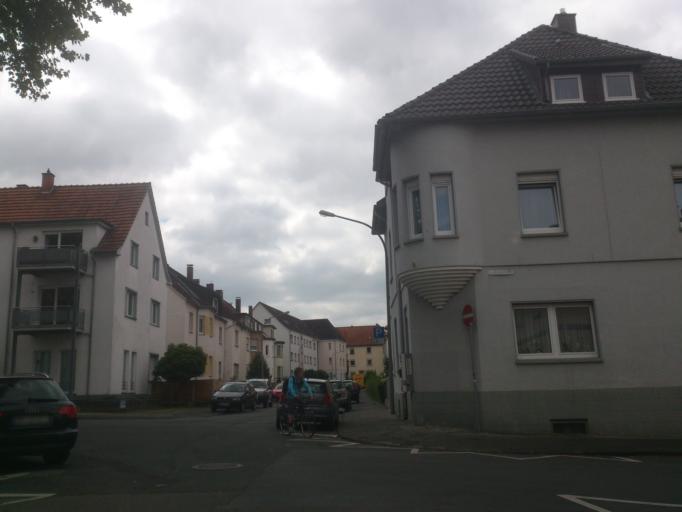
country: DE
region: North Rhine-Westphalia
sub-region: Regierungsbezirk Detmold
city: Paderborn
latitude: 51.7116
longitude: 8.7504
